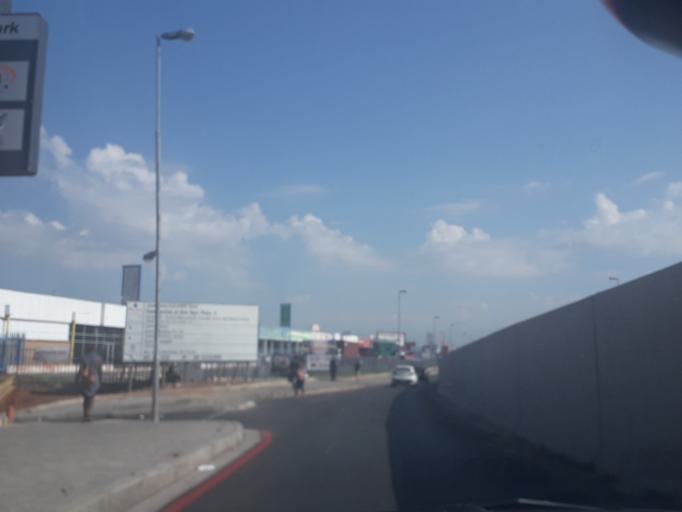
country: ZA
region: Gauteng
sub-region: City of Johannesburg Metropolitan Municipality
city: Modderfontein
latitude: -26.1190
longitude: 28.0842
